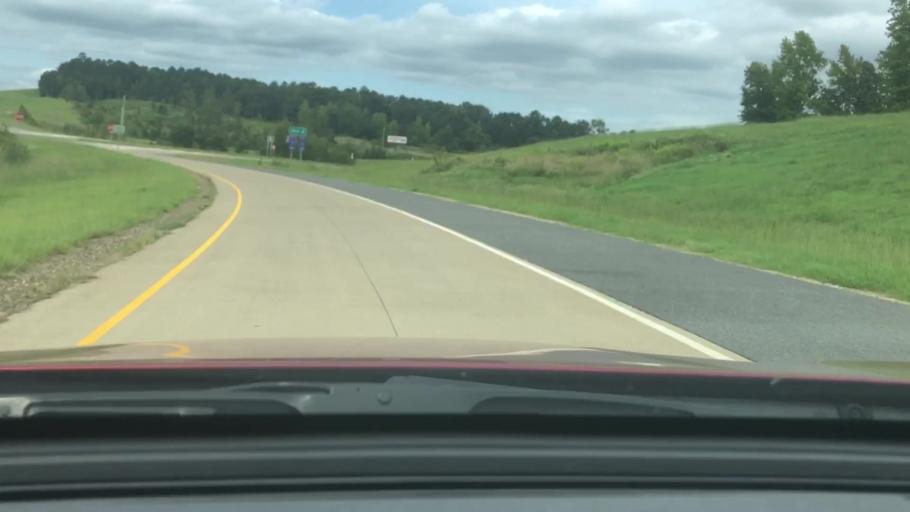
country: US
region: Louisiana
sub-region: Caddo Parish
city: Vivian
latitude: 32.9419
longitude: -93.8963
